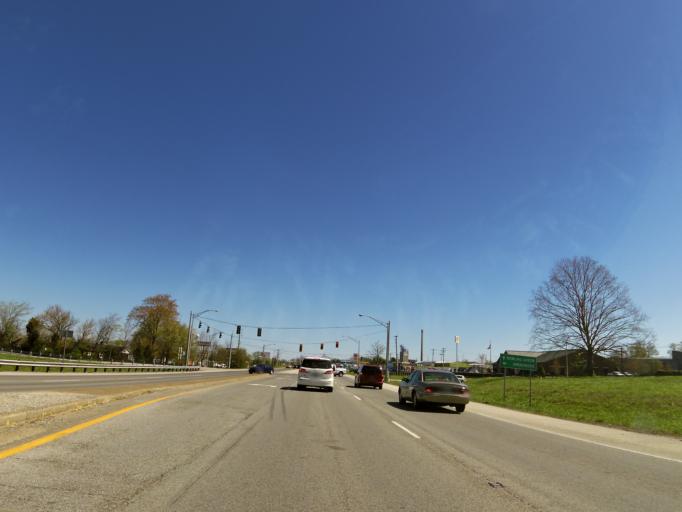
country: US
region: Kentucky
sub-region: Warren County
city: Bowling Green
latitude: 36.9574
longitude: -86.4969
